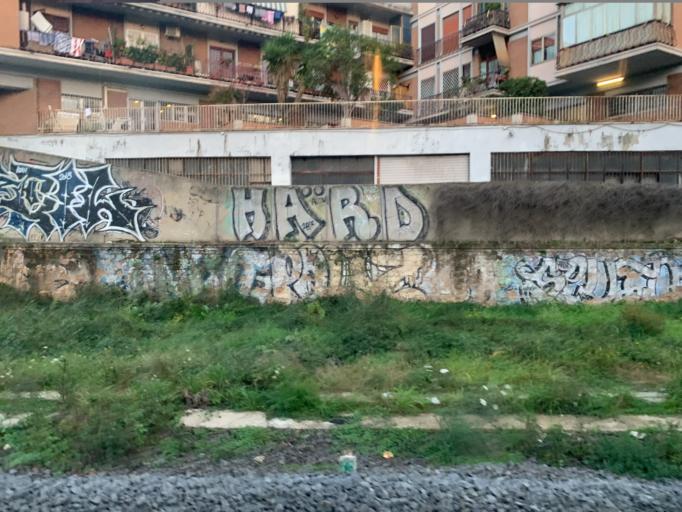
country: VA
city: Vatican City
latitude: 41.8691
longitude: 12.4606
